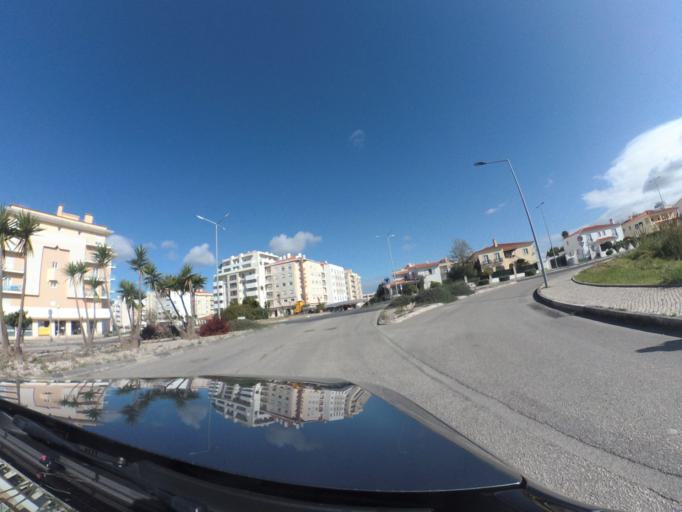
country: PT
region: Leiria
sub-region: Caldas da Rainha
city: Caldas da Rainha
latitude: 39.4125
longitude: -9.1364
